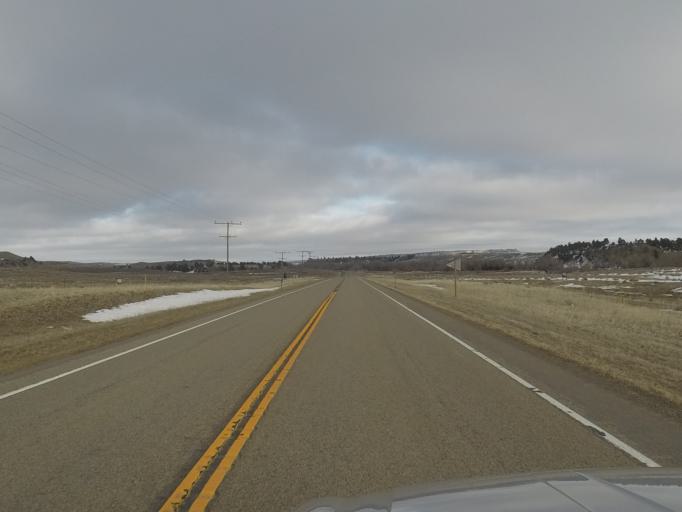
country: US
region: Montana
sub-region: Golden Valley County
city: Ryegate
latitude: 46.2999
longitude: -109.3239
